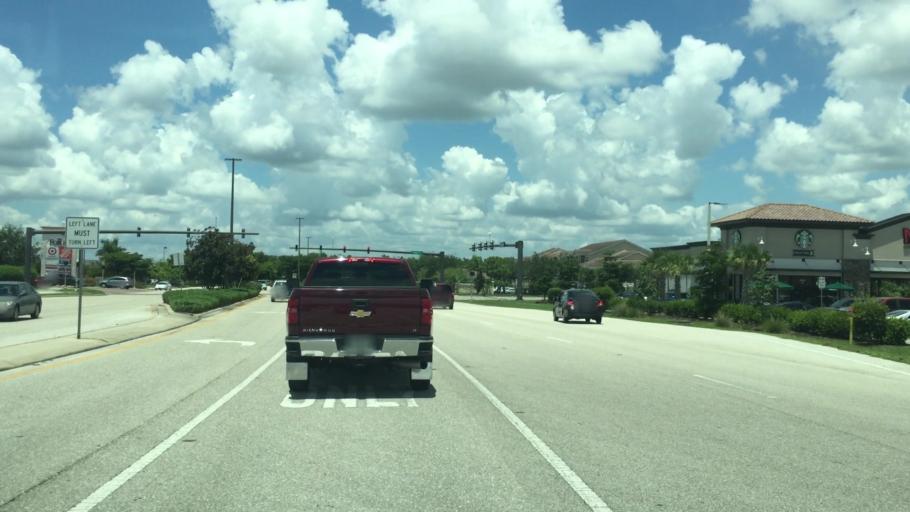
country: US
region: Florida
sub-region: Lee County
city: Fort Myers
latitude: 26.6148
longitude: -81.7965
